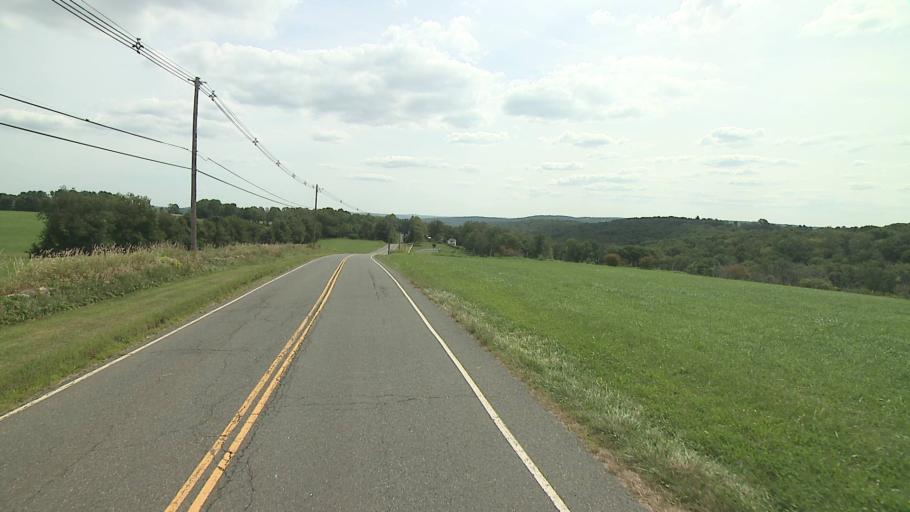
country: US
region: Connecticut
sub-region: Litchfield County
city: Bethlehem Village
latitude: 41.6114
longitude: -73.2448
